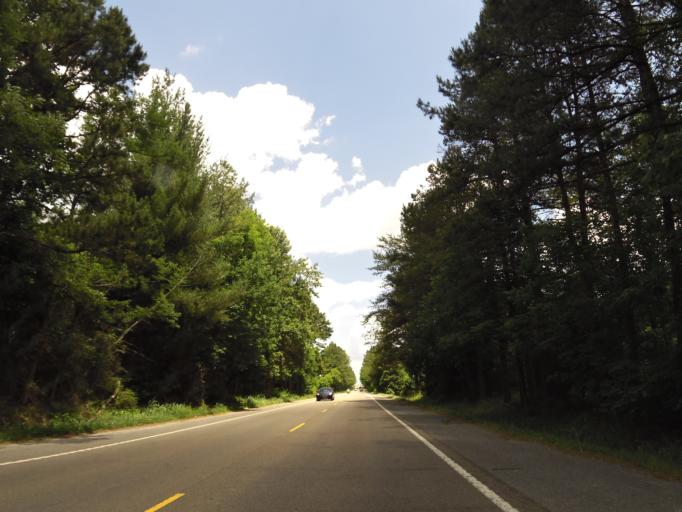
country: US
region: Tennessee
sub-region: Union County
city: Maynardville
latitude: 36.2192
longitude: -83.8557
